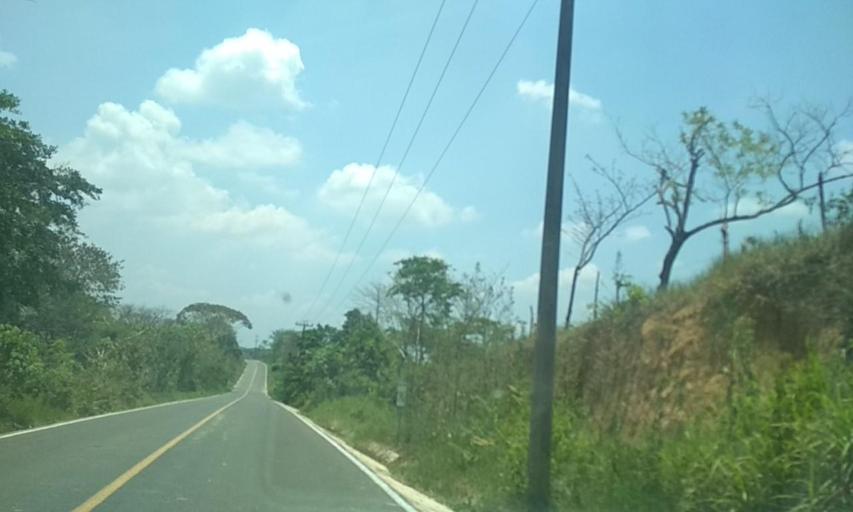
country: MX
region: Tabasco
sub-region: Huimanguillo
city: Francisco Rueda
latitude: 17.7610
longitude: -94.0578
